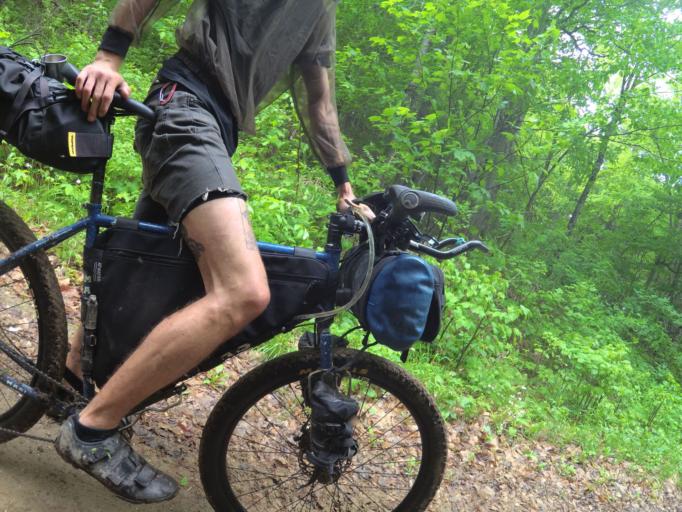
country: CA
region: Ontario
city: Renfrew
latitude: 45.1131
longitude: -76.8540
